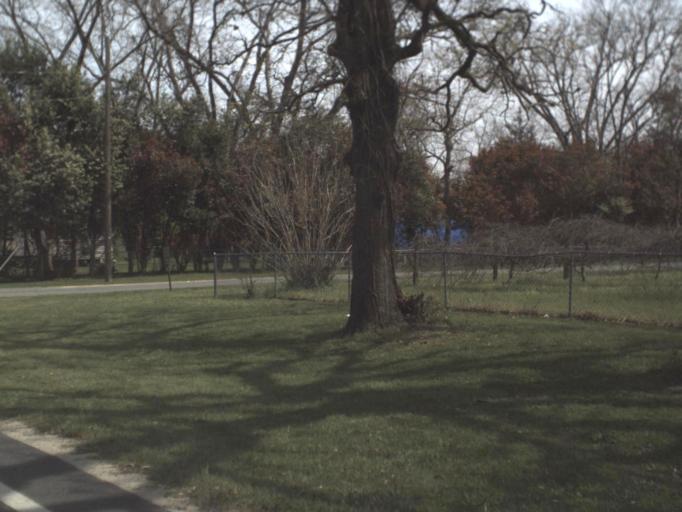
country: US
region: Florida
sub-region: Jackson County
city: Malone
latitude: 30.9579
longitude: -85.1675
